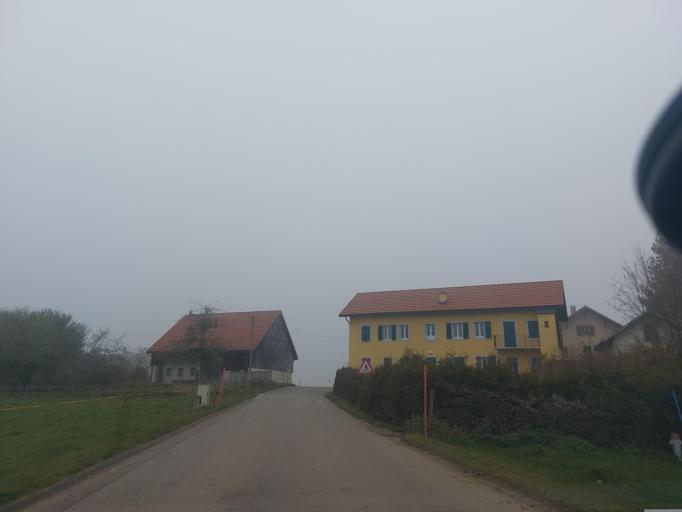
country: CH
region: Fribourg
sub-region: Veveyse District
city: Chatel-Saint-Denis
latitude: 46.5708
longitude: 6.8916
